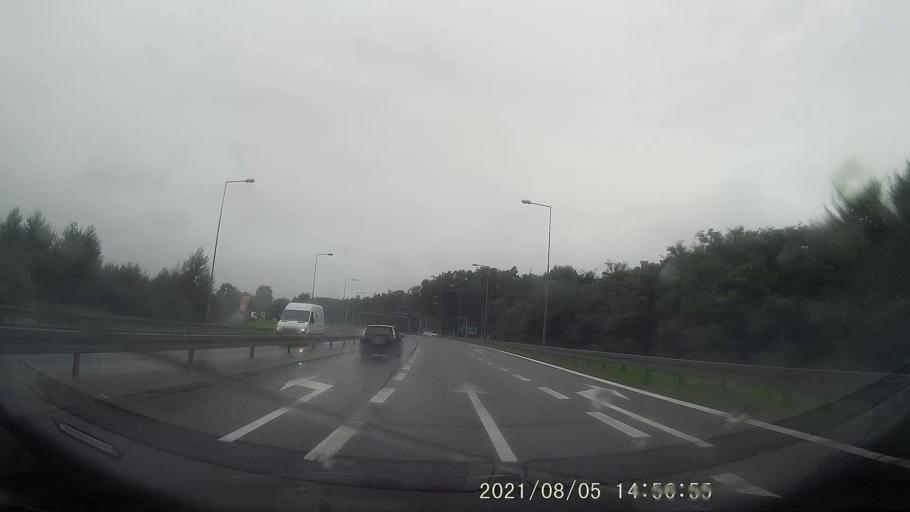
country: PL
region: Opole Voivodeship
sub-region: Powiat nyski
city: Otmuchow
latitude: 50.4585
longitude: 17.1697
